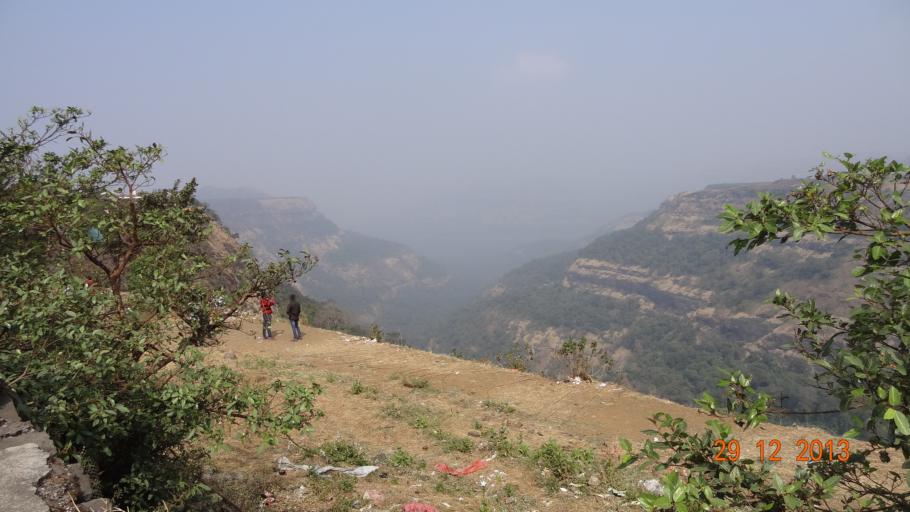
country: IN
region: Maharashtra
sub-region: Raigarh
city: Khopoli
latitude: 18.7688
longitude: 73.3675
